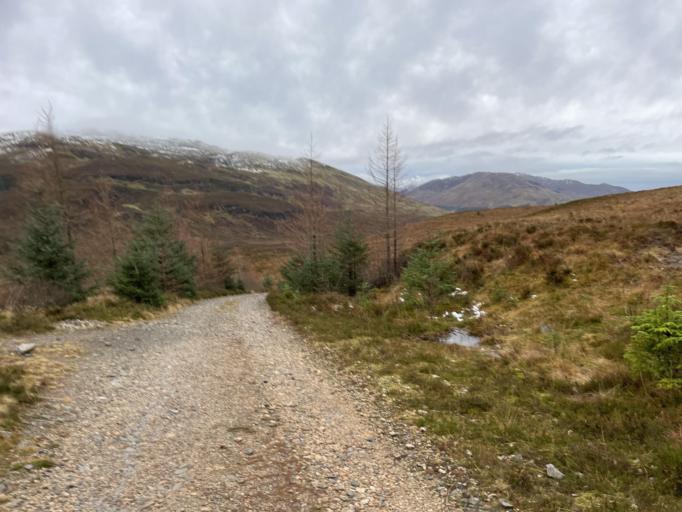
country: GB
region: Scotland
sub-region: Highland
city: Fort William
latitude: 56.8088
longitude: -5.0950
